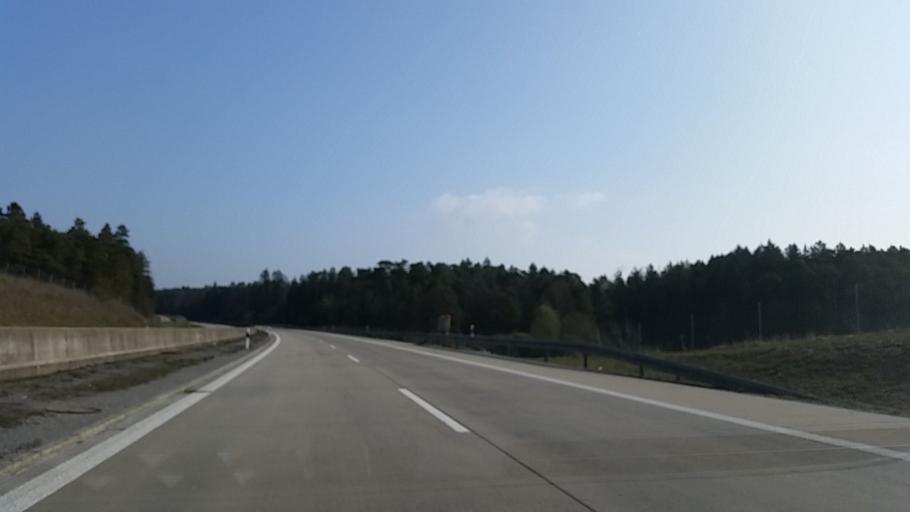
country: DE
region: Bavaria
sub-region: Regierungsbezirk Unterfranken
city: Strahlungen
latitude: 50.2768
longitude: 10.2554
